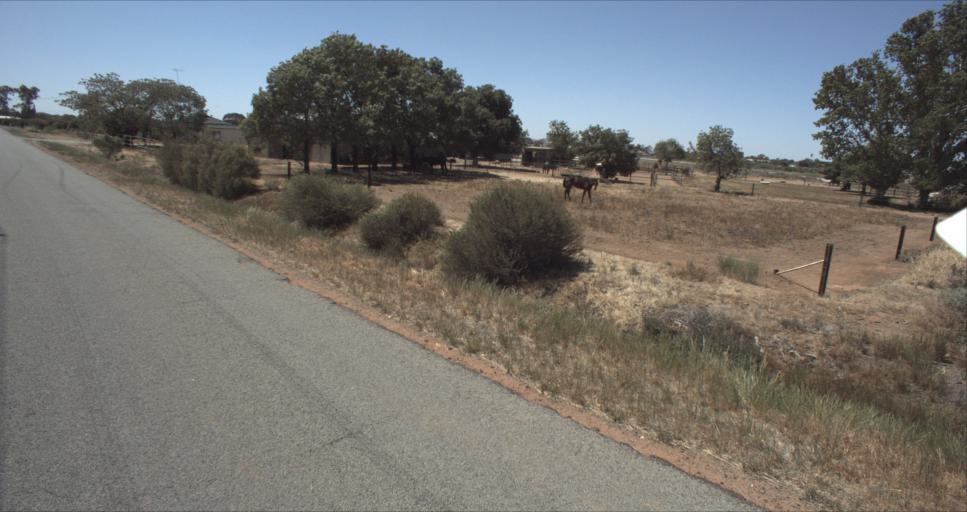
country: AU
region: New South Wales
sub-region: Leeton
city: Leeton
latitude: -34.5358
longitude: 146.3972
